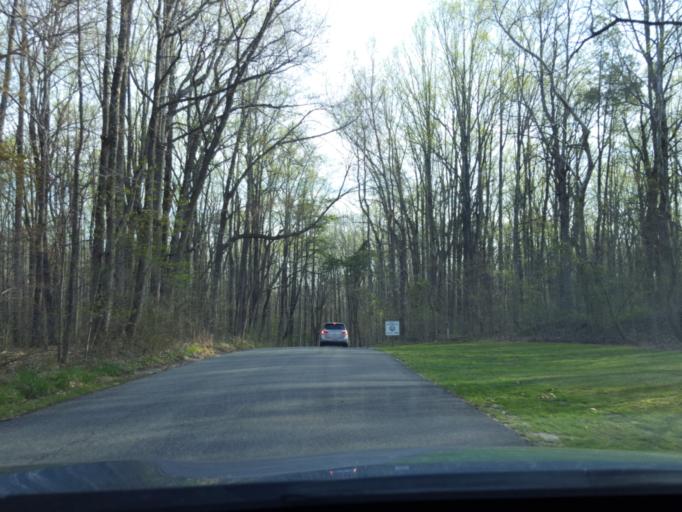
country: US
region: Maryland
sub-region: Prince George's County
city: Croom
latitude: 38.7577
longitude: -76.7254
